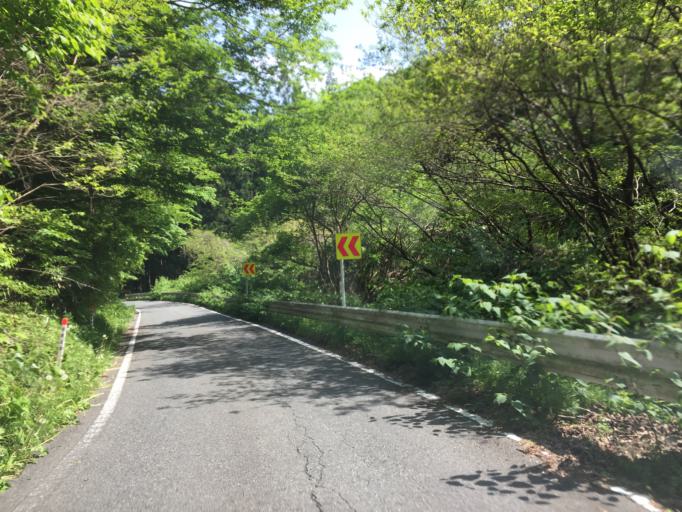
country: JP
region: Fukushima
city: Ishikawa
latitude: 36.9999
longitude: 140.6070
